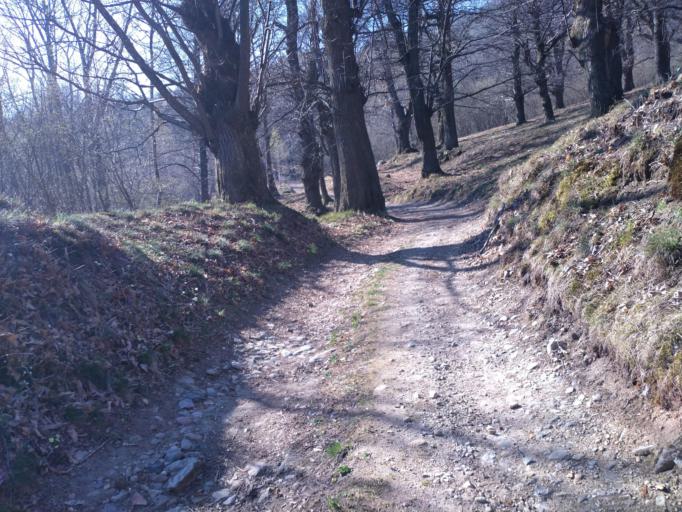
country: IT
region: Lombardy
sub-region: Provincia di Como
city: Rezzago
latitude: 45.8569
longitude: 9.2383
